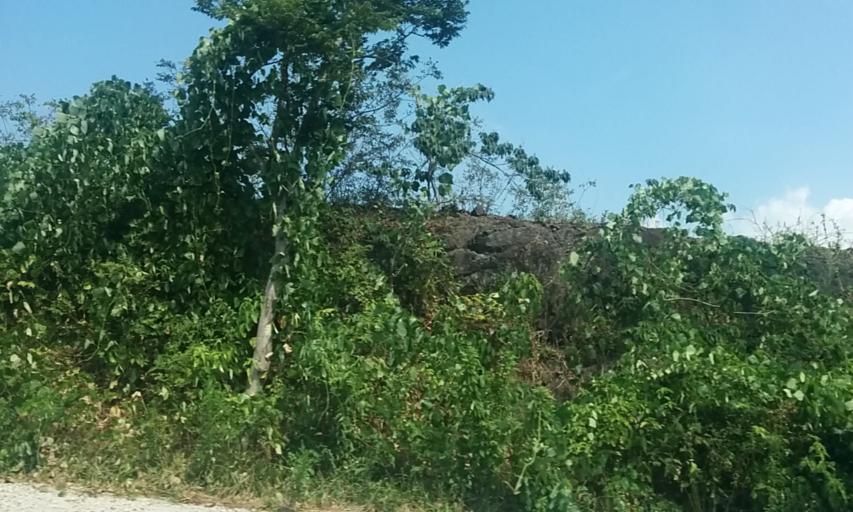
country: JP
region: Kyoto
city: Fukuchiyama
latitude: 35.3809
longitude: 135.1616
